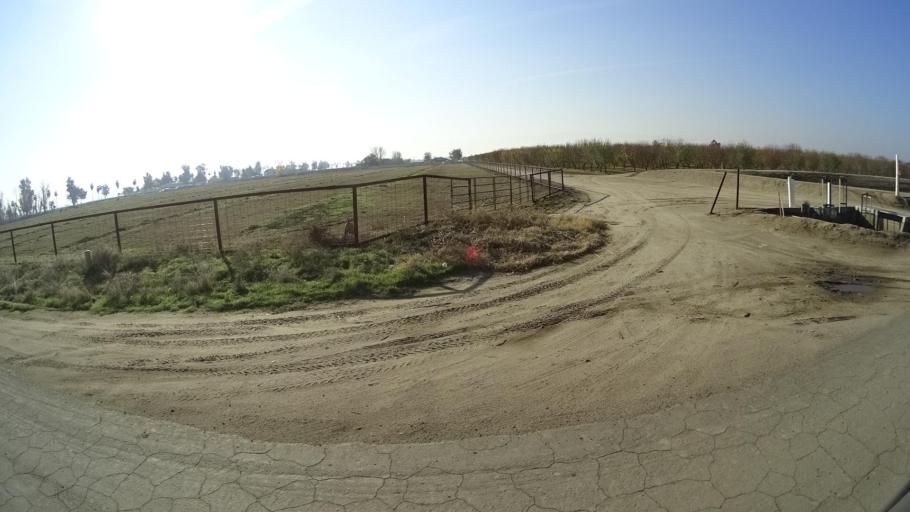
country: US
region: California
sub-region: Kern County
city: Greenfield
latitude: 35.2240
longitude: -119.0079
